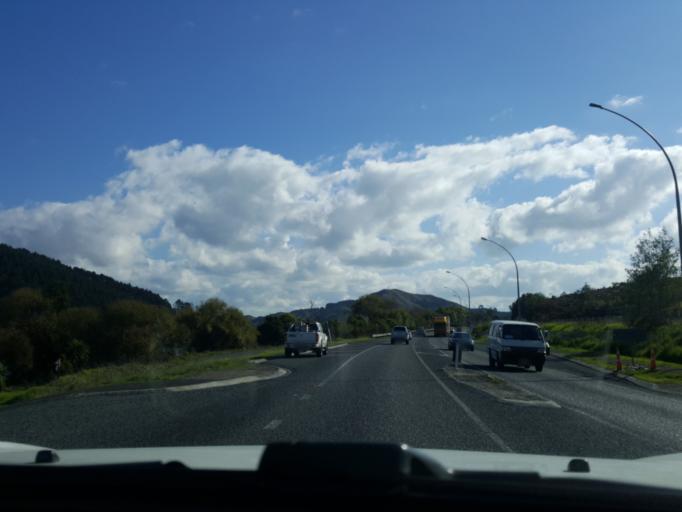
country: NZ
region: Waikato
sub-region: Waikato District
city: Ngaruawahia
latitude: -37.6081
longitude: 175.1826
